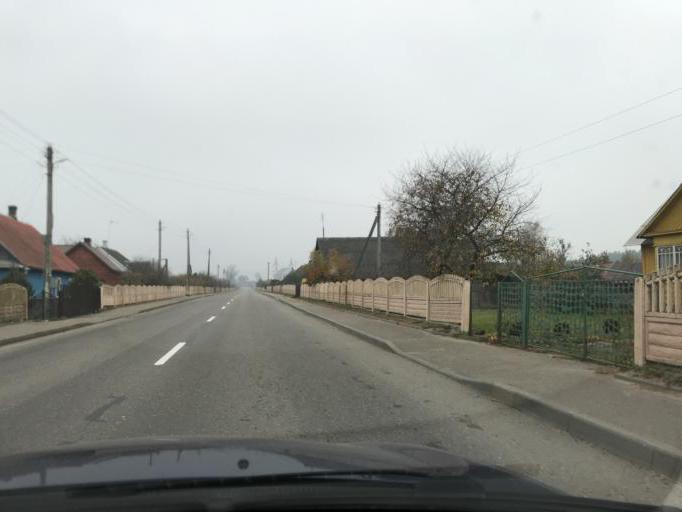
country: BY
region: Grodnenskaya
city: Hrodna
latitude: 53.8198
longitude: 23.8680
